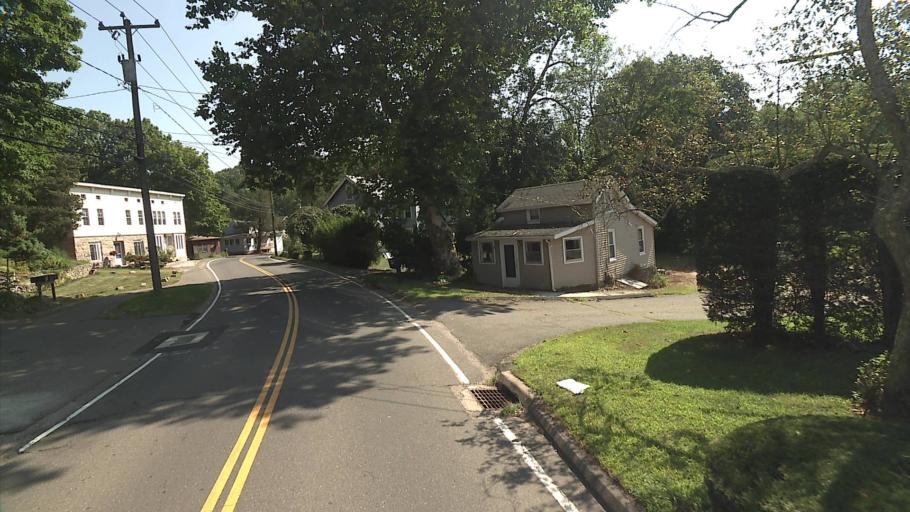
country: US
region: Connecticut
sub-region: New Haven County
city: North Branford
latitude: 41.2742
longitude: -72.7505
